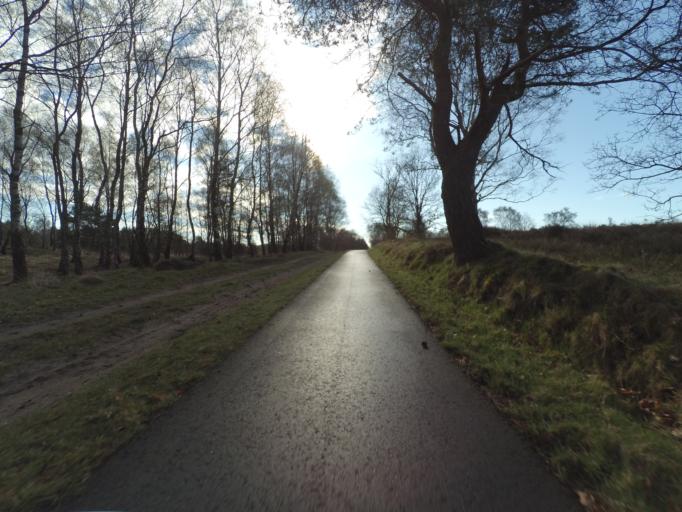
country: NL
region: Gelderland
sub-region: Gemeente Apeldoorn
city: Uddel
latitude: 52.1996
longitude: 5.8599
